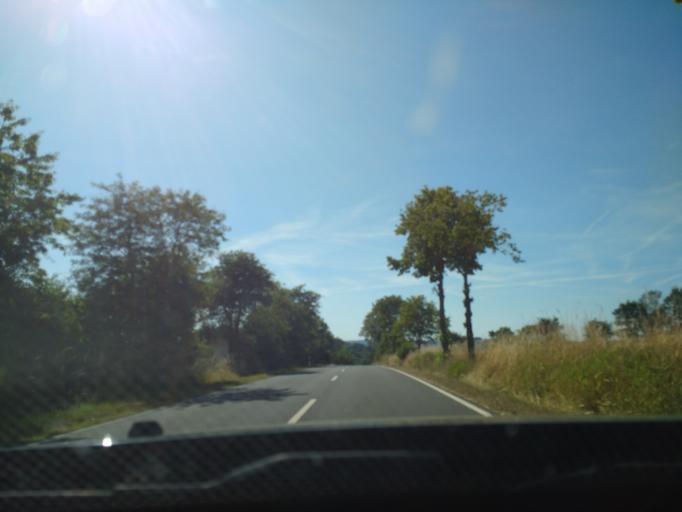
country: DE
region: Rheinland-Pfalz
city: Brockscheid
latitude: 50.1441
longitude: 6.8360
